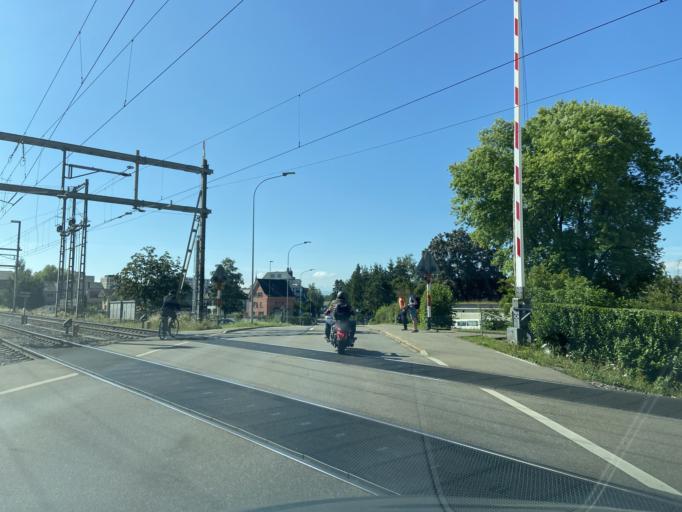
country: CH
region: Zurich
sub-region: Bezirk Uster
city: Uster / Gschwader
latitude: 47.3539
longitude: 8.7127
